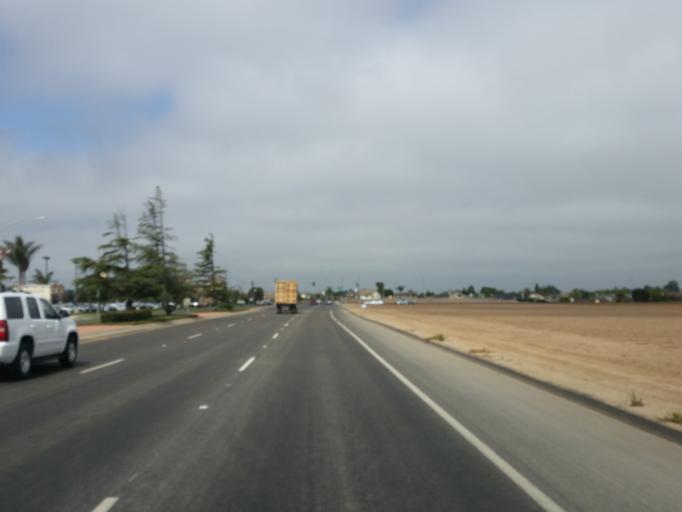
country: US
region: California
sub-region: Santa Barbara County
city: Santa Maria
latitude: 34.9237
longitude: -120.4231
